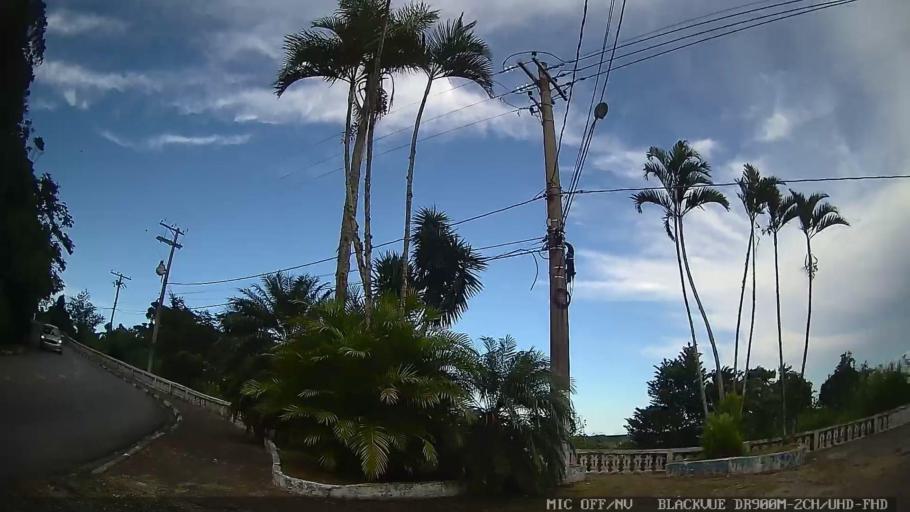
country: BR
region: Sao Paulo
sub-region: Iguape
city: Iguape
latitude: -24.7058
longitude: -47.5478
